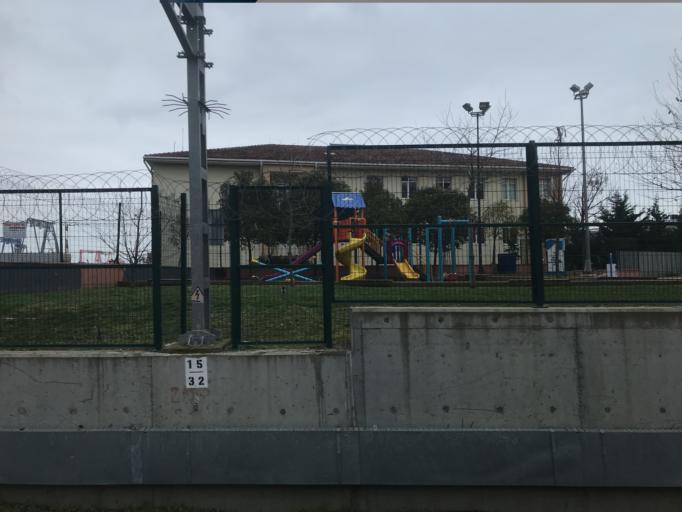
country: TR
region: Istanbul
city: Pendik
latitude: 40.8568
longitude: 29.2853
